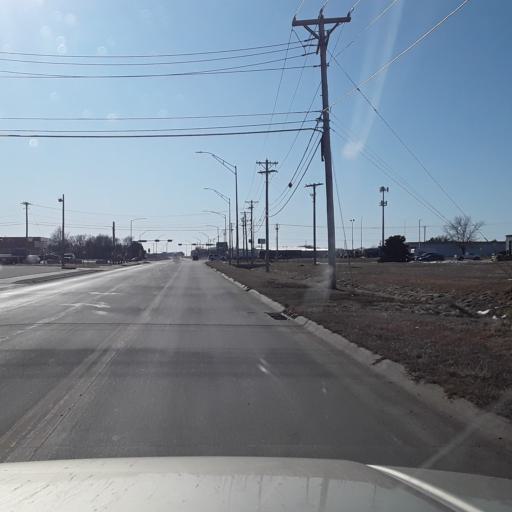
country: US
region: Nebraska
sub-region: Adams County
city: Hastings
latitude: 40.5703
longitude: -98.4021
